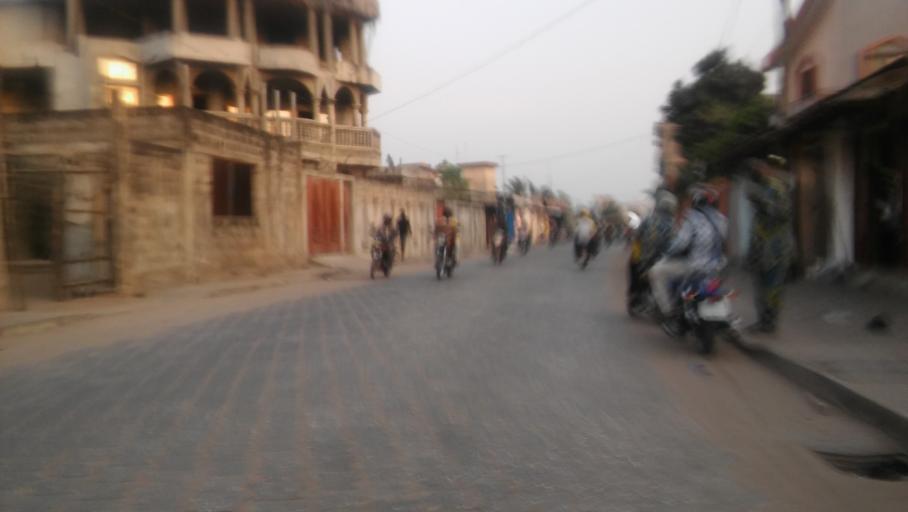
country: BJ
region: Atlantique
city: Abomey-Calavi
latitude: 6.3952
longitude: 2.3506
